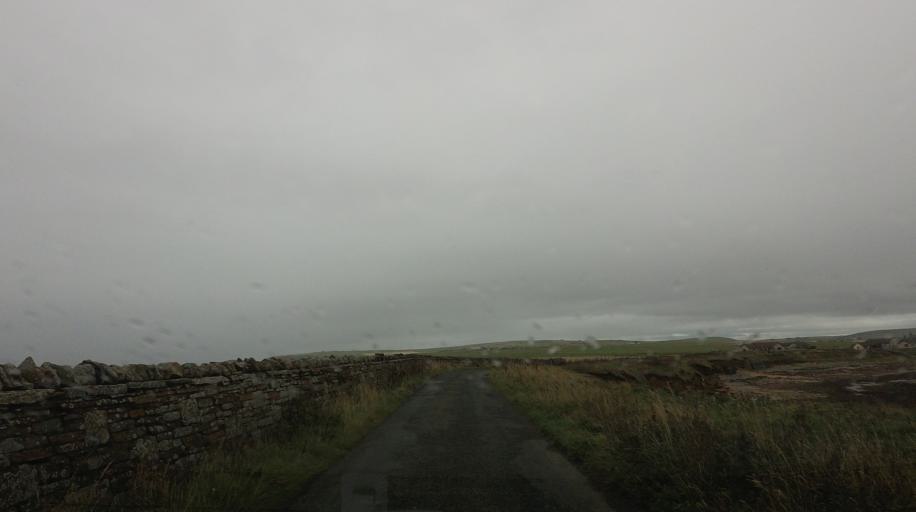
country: GB
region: Scotland
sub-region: Orkney Islands
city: Stromness
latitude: 59.1336
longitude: -3.3209
